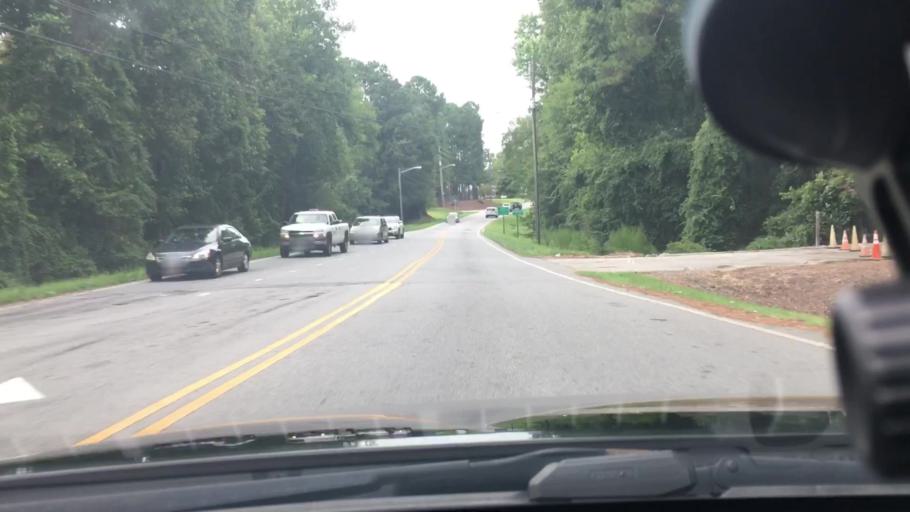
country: US
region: North Carolina
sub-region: Pitt County
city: Windsor
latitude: 35.5718
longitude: -77.3417
